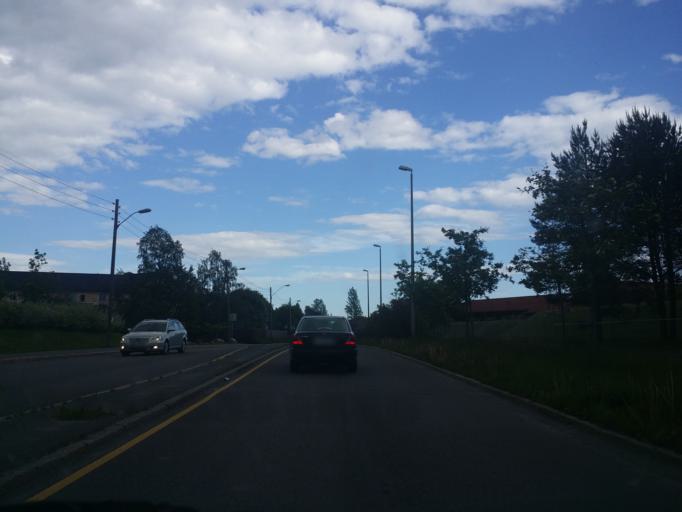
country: NO
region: Oslo
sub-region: Oslo
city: Sjolyststranda
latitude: 59.9448
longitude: 10.6570
